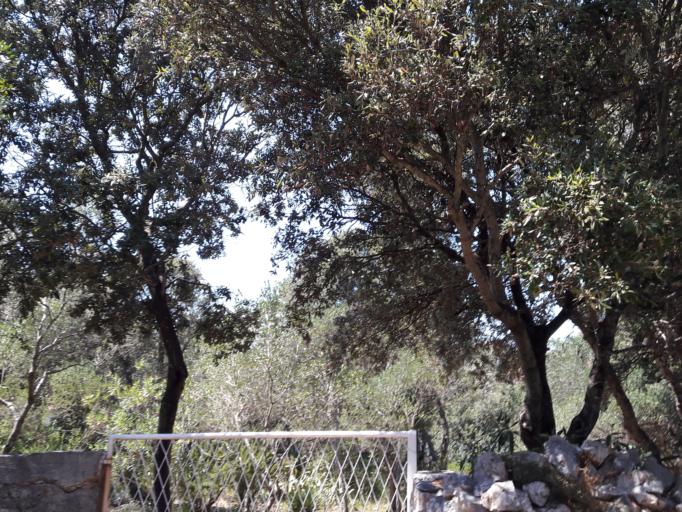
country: HR
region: Licko-Senjska
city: Novalja
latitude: 44.3679
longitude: 14.6937
